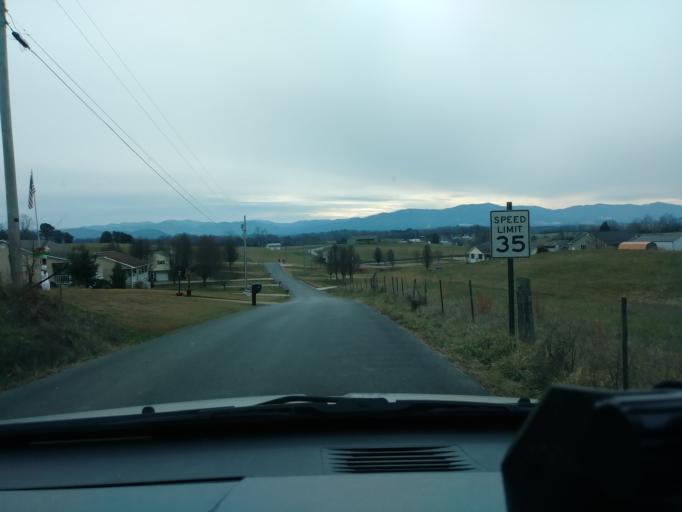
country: US
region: Tennessee
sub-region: Greene County
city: Greeneville
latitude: 36.0959
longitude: -82.8941
